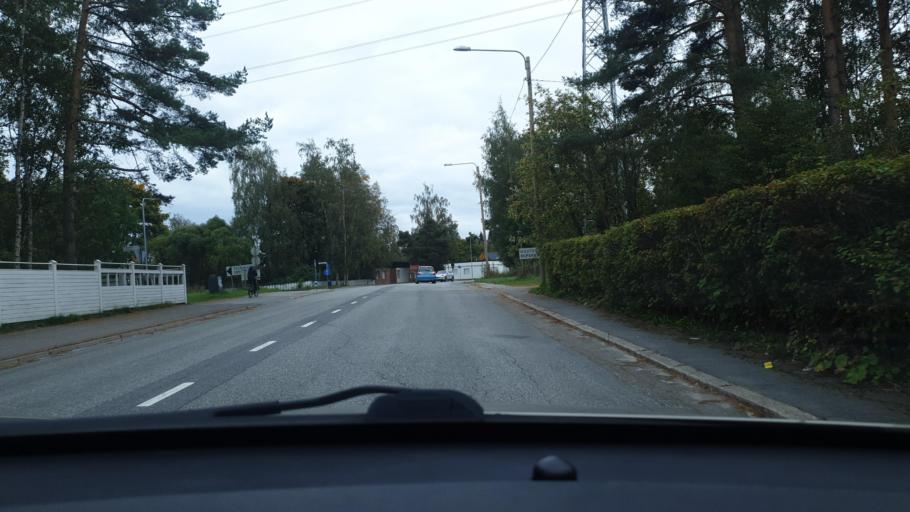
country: FI
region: Ostrobothnia
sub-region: Vaasa
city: Korsholm
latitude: 63.0976
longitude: 21.6688
